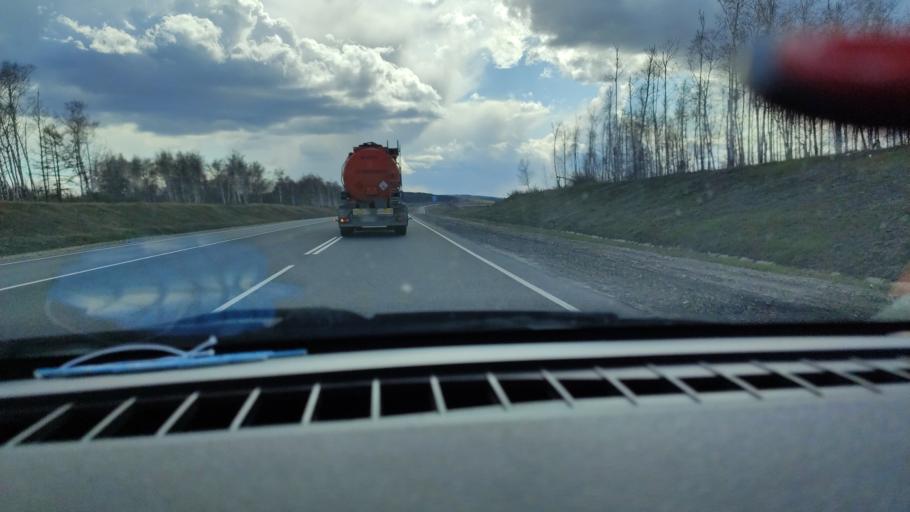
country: RU
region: Saratov
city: Khvalynsk
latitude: 52.5552
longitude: 48.0809
